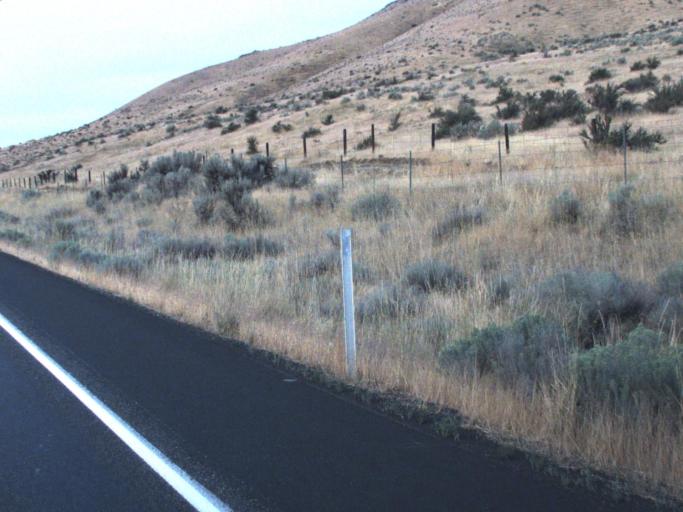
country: US
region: Washington
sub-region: Yakima County
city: Toppenish
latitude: 46.1504
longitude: -120.5109
